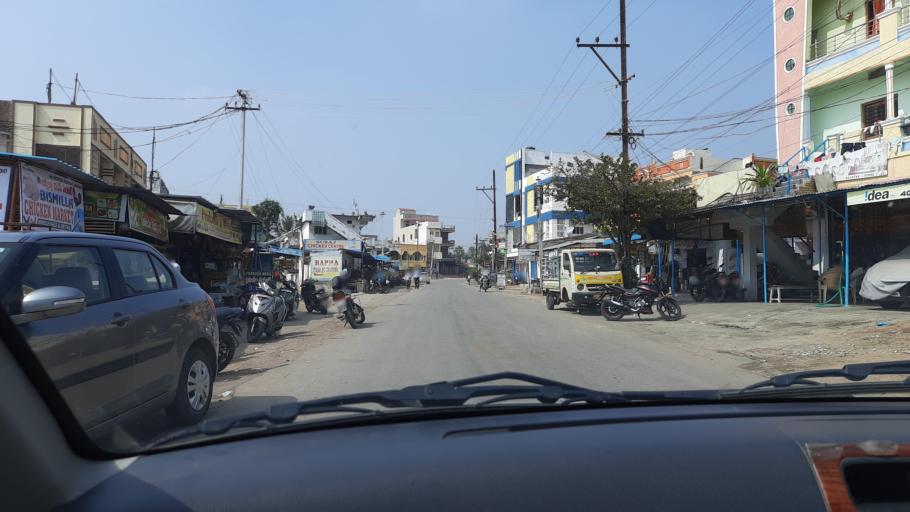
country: IN
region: Telangana
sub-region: Rangareddi
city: Lal Bahadur Nagar
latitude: 17.2710
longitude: 78.6704
